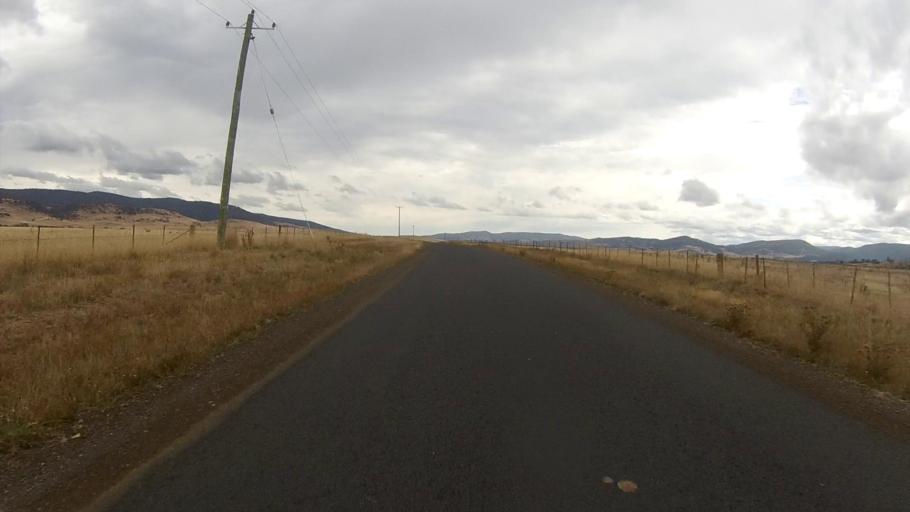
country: AU
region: Tasmania
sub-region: Northern Midlands
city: Evandale
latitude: -41.8258
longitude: 147.7711
